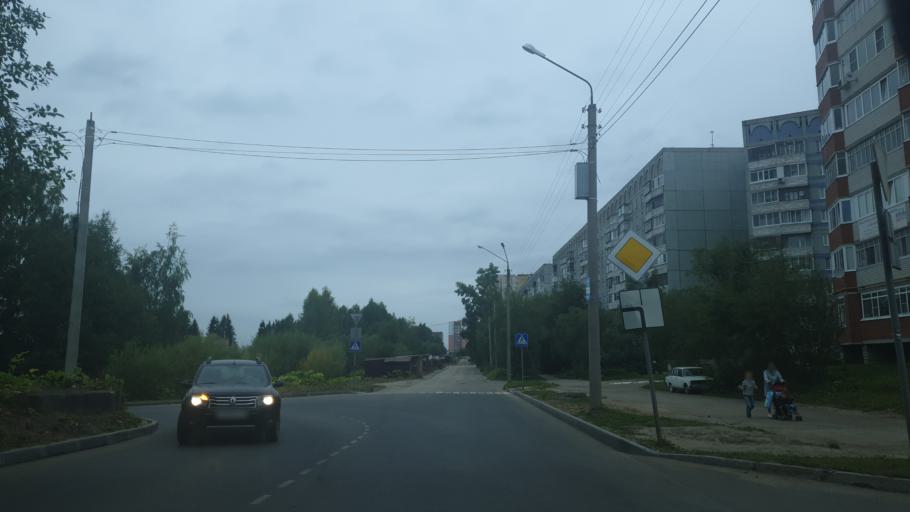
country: RU
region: Komi Republic
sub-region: Syktyvdinskiy Rayon
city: Syktyvkar
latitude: 61.6961
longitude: 50.8068
